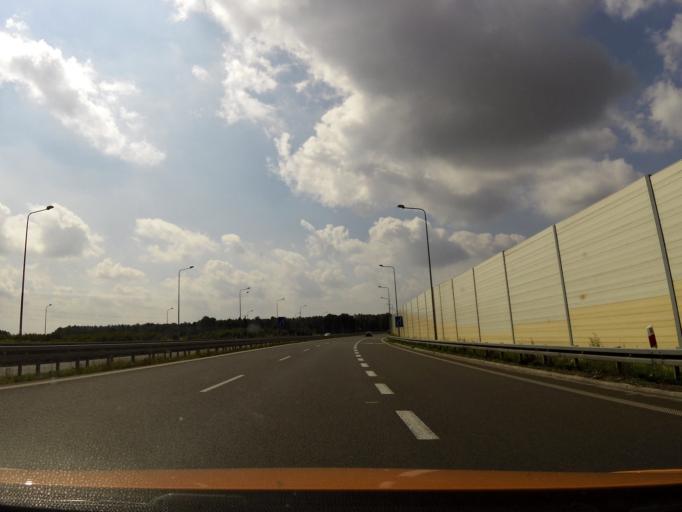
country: PL
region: West Pomeranian Voivodeship
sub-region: Powiat goleniowski
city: Nowogard
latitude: 53.6554
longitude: 15.0778
